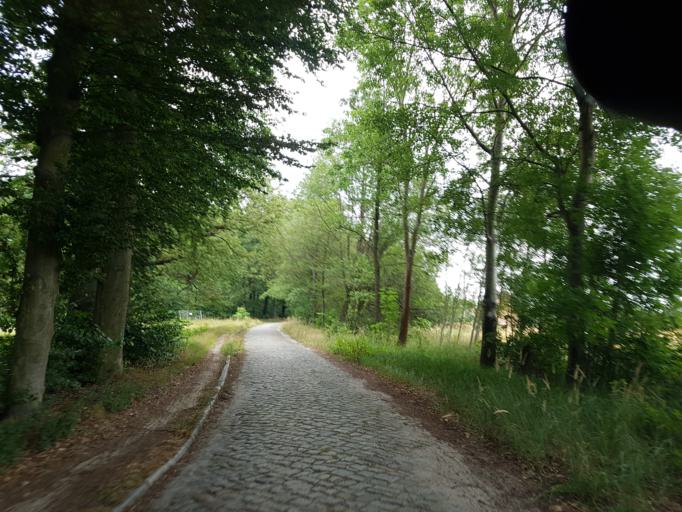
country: DE
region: Brandenburg
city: Sallgast
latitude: 51.5842
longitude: 13.8451
